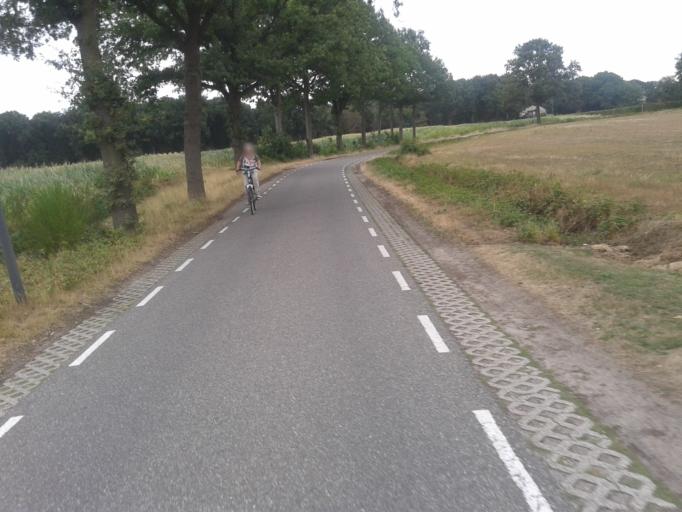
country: NL
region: North Brabant
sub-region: Gemeente Oisterwijk
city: Oisterwijk
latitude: 51.5520
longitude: 5.1921
